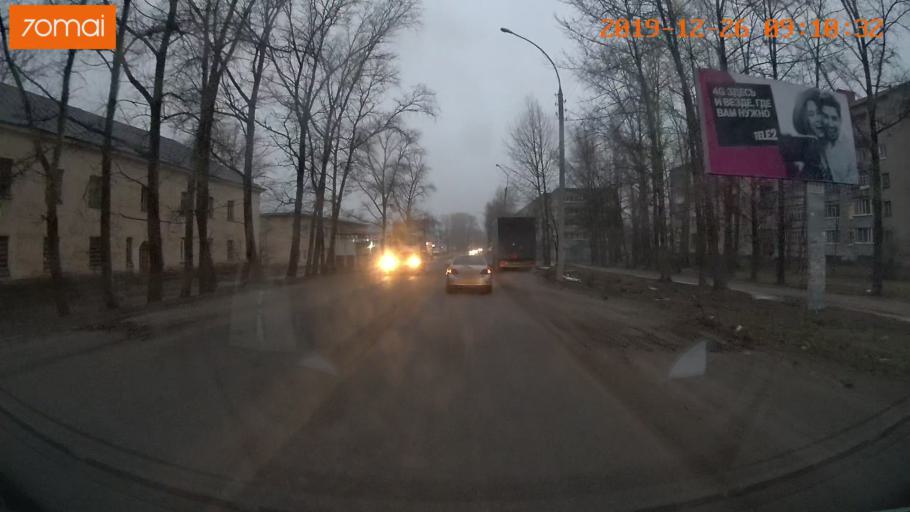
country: RU
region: Vologda
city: Gryazovets
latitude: 58.8716
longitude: 40.2526
